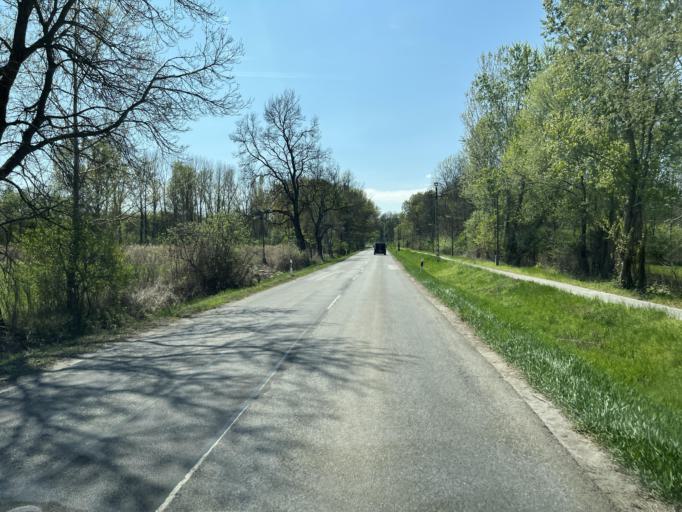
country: HU
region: Pest
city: Dabas
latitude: 47.2213
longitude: 19.2808
